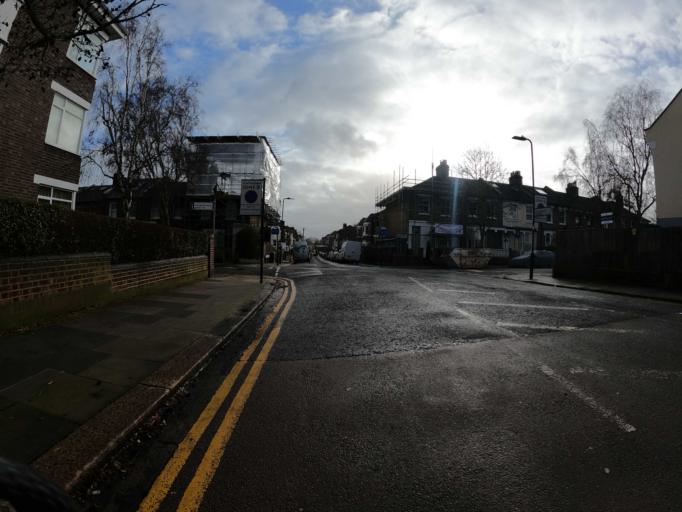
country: GB
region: England
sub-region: Greater London
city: Acton
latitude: 51.5106
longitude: -0.2634
